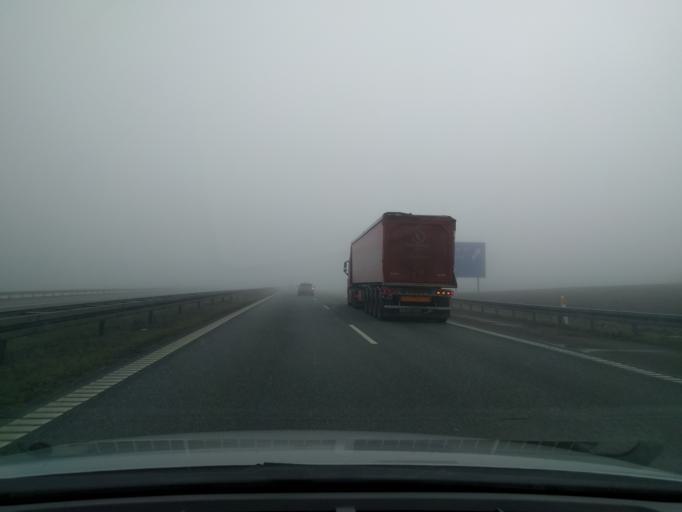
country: DK
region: Zealand
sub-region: Slagelse Kommune
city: Forlev
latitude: 55.3790
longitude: 11.3214
